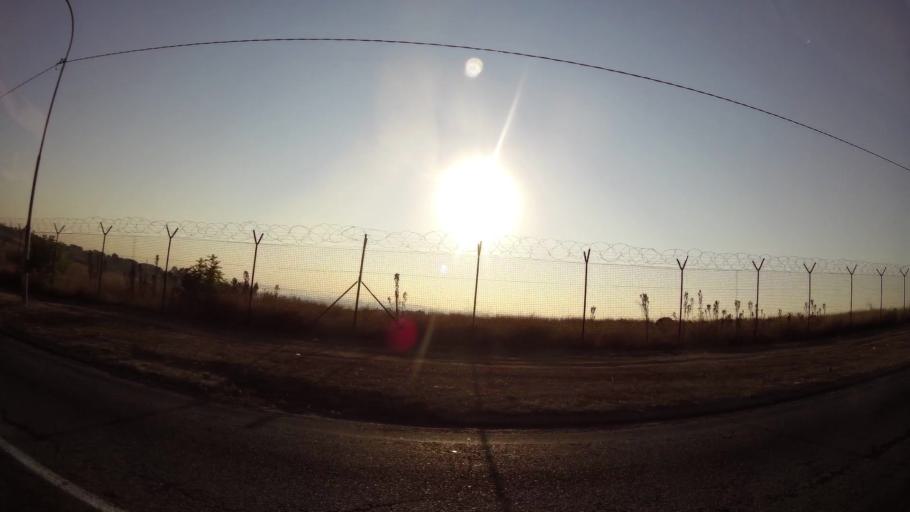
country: ZA
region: Gauteng
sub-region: City of Johannesburg Metropolitan Municipality
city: Modderfontein
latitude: -26.0726
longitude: 28.0973
